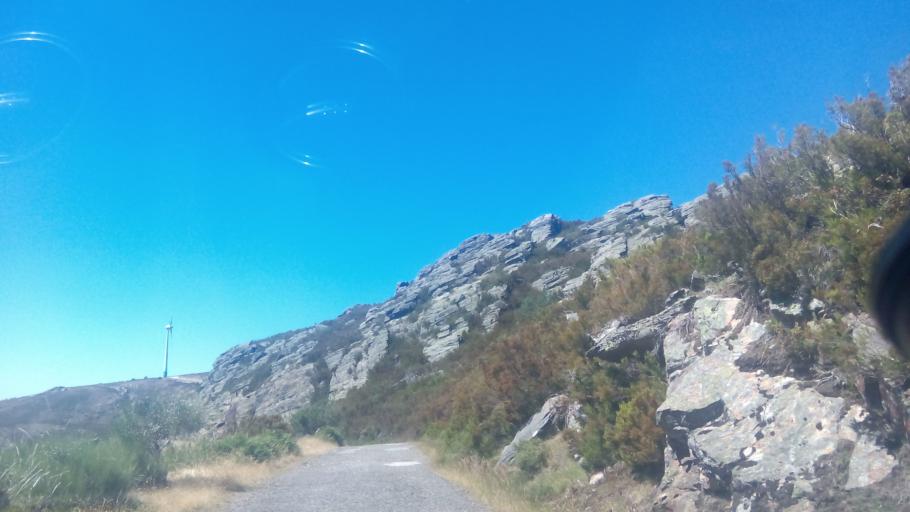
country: PT
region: Vila Real
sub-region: Mesao Frio
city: Mesao Frio
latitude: 41.2602
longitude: -7.8972
